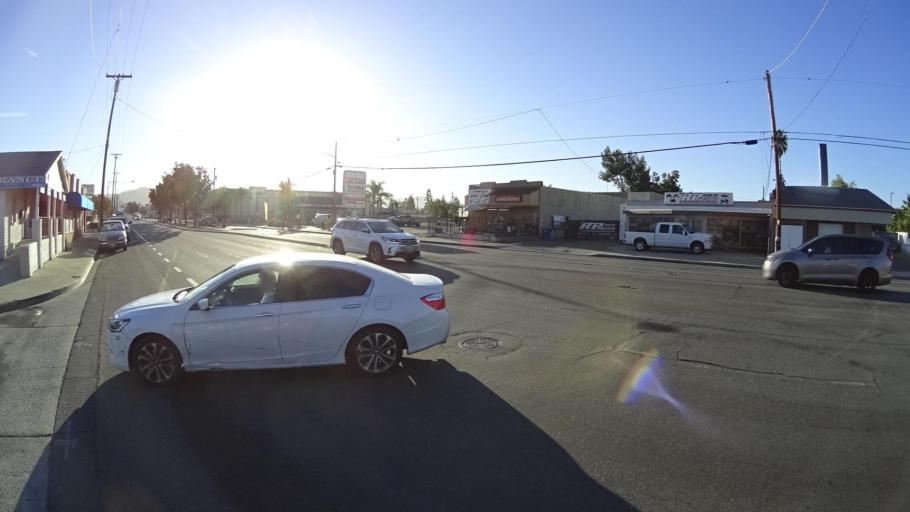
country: US
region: California
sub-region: San Diego County
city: Bostonia
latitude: 32.8078
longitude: -116.9379
